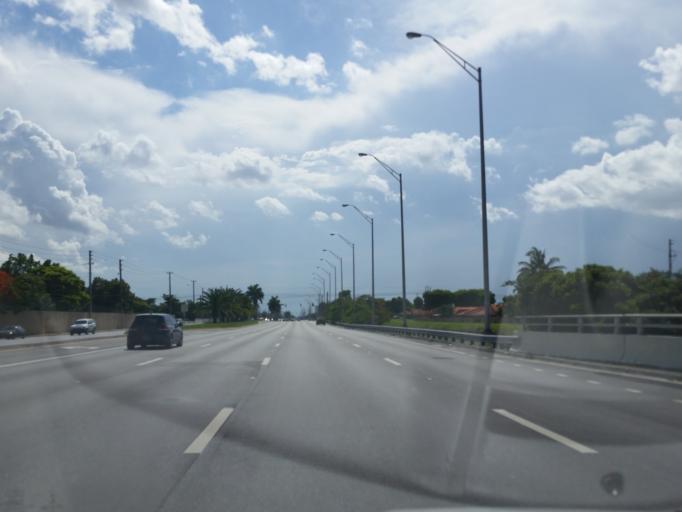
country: US
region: Florida
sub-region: Miami-Dade County
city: Fountainebleau
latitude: 25.7619
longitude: -80.3455
